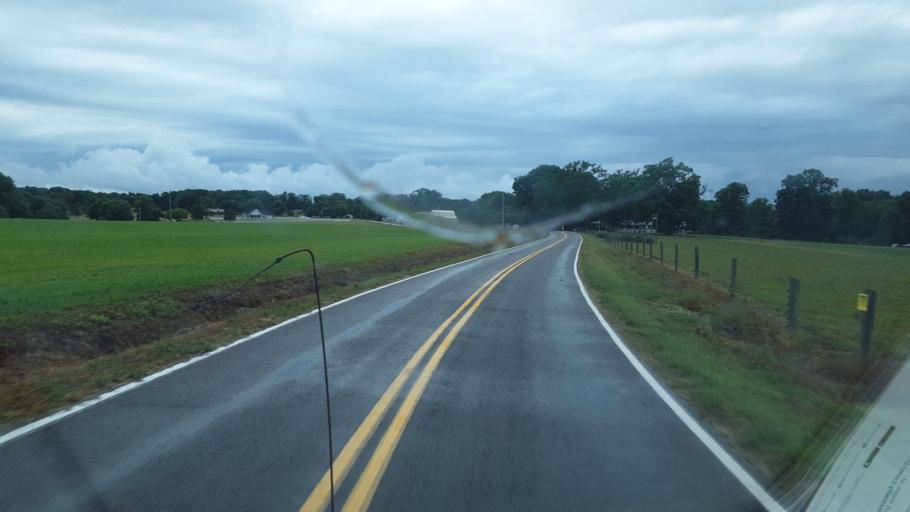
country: US
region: North Carolina
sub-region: Yadkin County
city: Jonesville
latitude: 36.0830
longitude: -80.8490
